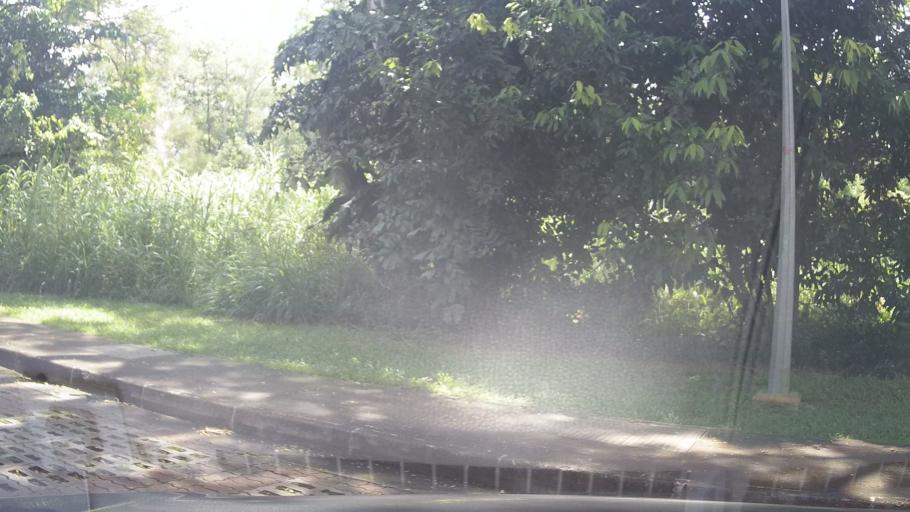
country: MY
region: Johor
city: Kampung Pasir Gudang Baru
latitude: 1.3775
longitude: 103.9489
